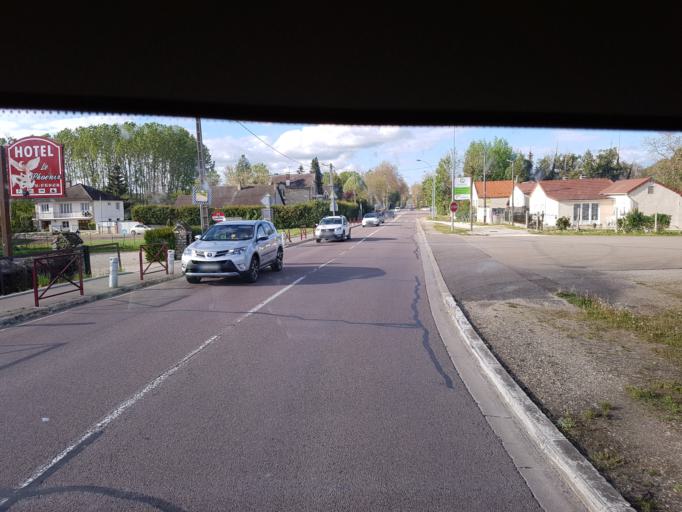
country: FR
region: Bourgogne
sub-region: Departement de l'Yonne
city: Saint-Florentin
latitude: 47.9836
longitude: 3.7327
